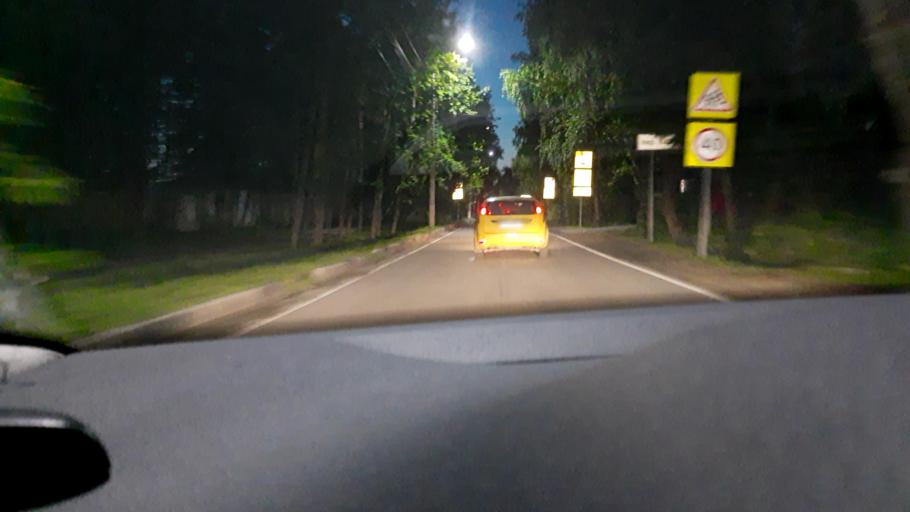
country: RU
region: Moskovskaya
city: Opalikha
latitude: 55.8323
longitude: 37.2504
